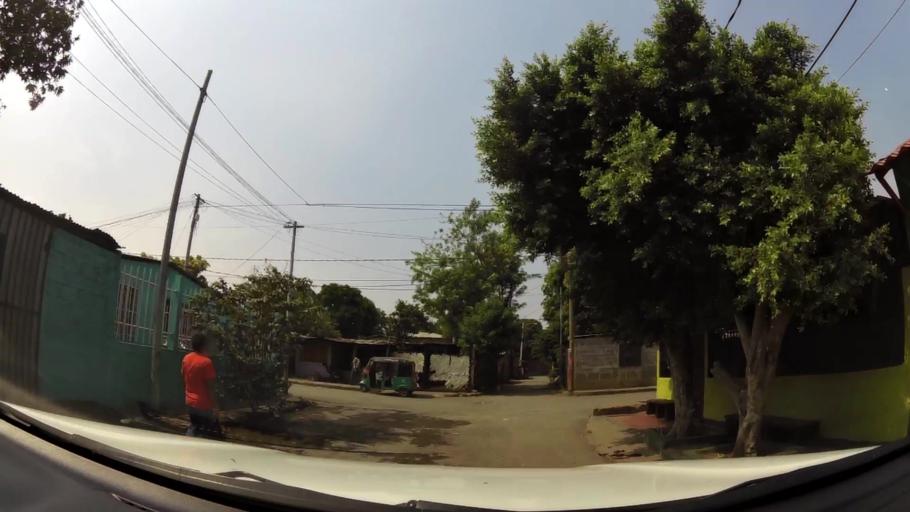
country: NI
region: Managua
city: Ciudad Sandino
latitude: 12.1281
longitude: -86.3151
